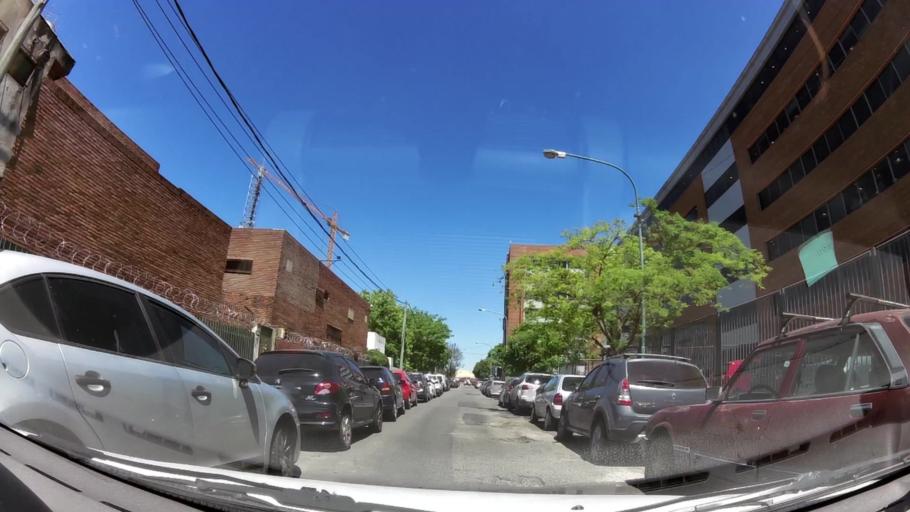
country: AR
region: Buenos Aires
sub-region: Partido de Vicente Lopez
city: Olivos
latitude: -34.5139
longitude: -58.5173
